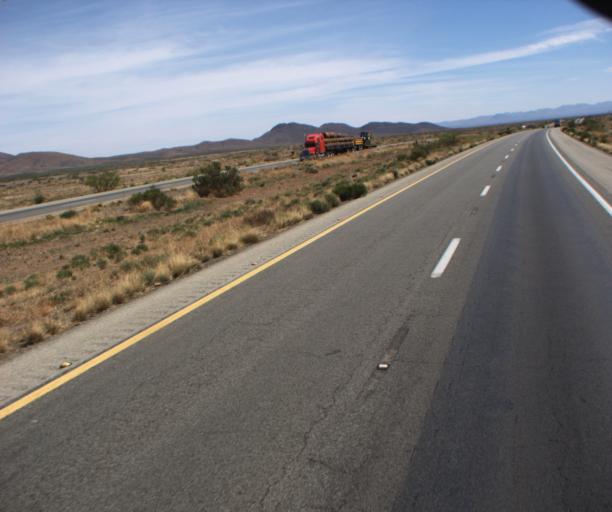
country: US
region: Arizona
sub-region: Cochise County
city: Willcox
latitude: 32.3622
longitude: -109.6499
